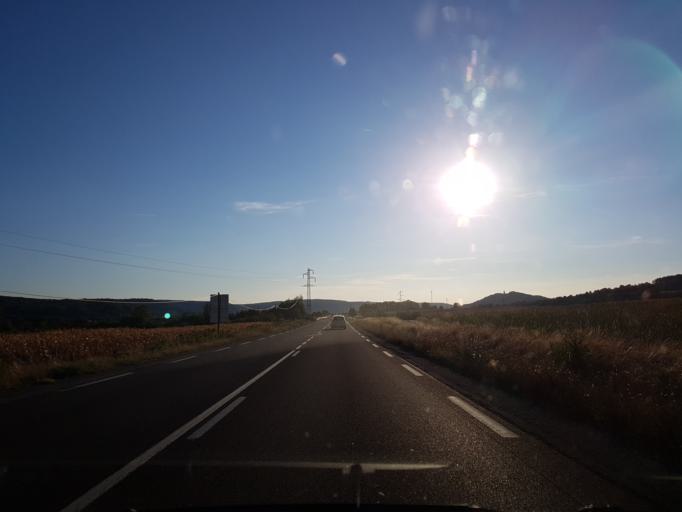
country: FR
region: Franche-Comte
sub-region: Departement de la Haute-Saone
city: Frotey-les-Vesoul
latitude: 47.6244
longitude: 6.2039
